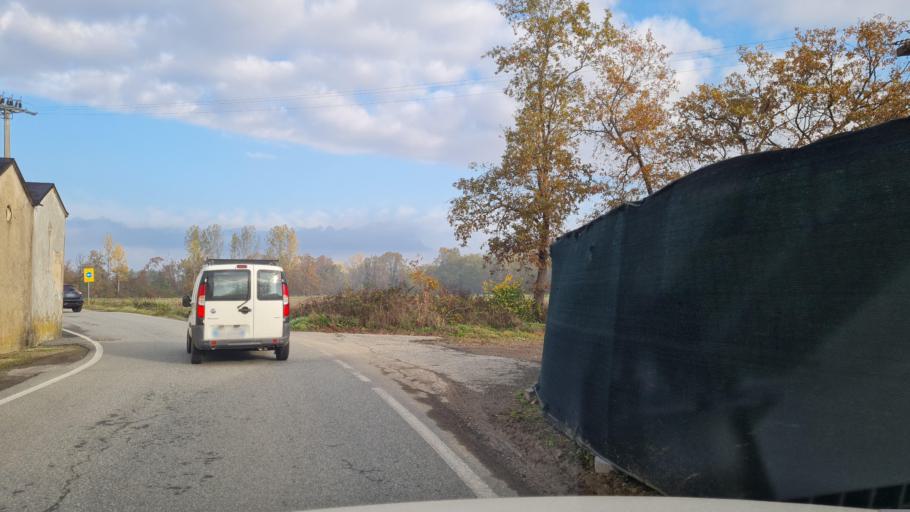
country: IT
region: Piedmont
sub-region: Provincia di Biella
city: Castelletto Cervo
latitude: 45.5159
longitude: 8.2302
